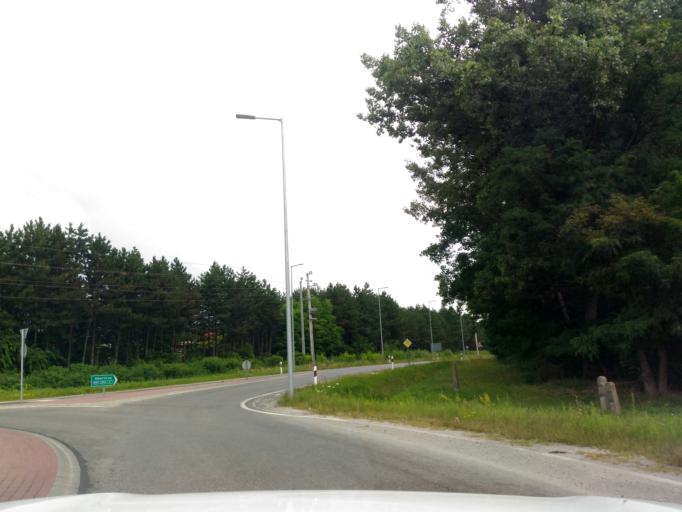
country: HU
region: Pest
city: Ujhartyan
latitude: 47.2128
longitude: 19.3947
